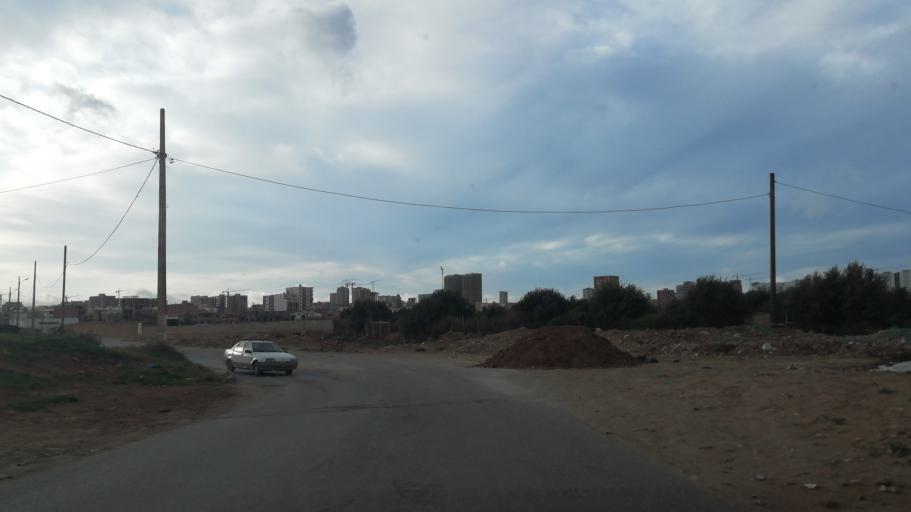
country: DZ
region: Oran
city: Bir el Djir
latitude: 35.7172
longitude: -0.5613
